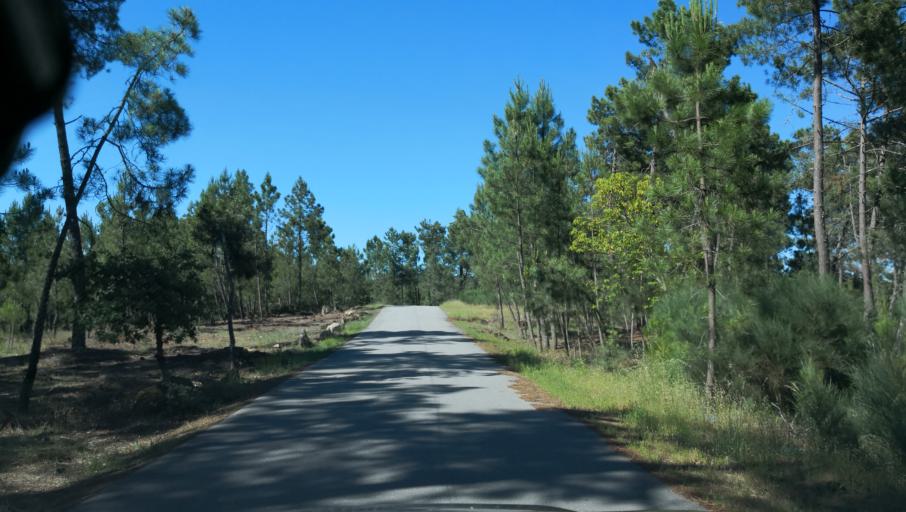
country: PT
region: Vila Real
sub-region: Vila Real
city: Vila Real
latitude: 41.2941
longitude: -7.6716
